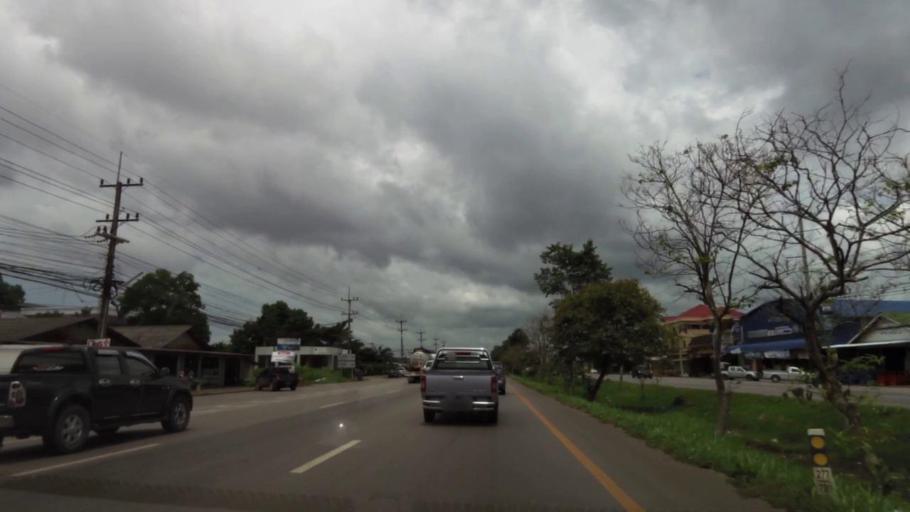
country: TH
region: Rayong
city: Klaeng
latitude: 12.7795
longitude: 101.7295
